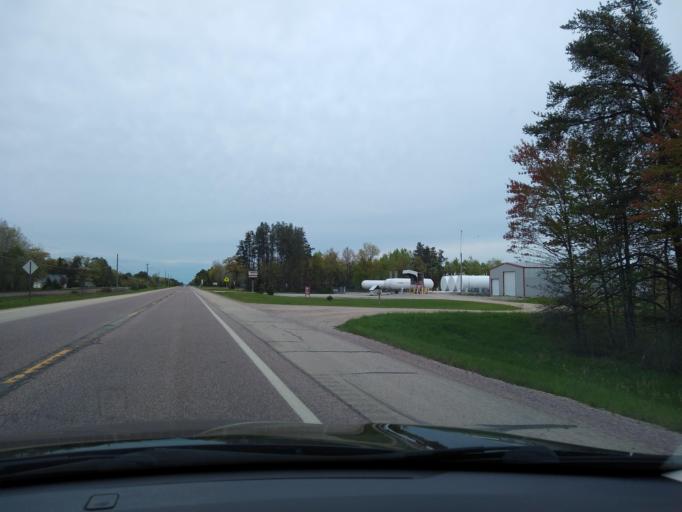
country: US
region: Michigan
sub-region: Delta County
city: Gladstone
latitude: 45.8606
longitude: -87.0624
